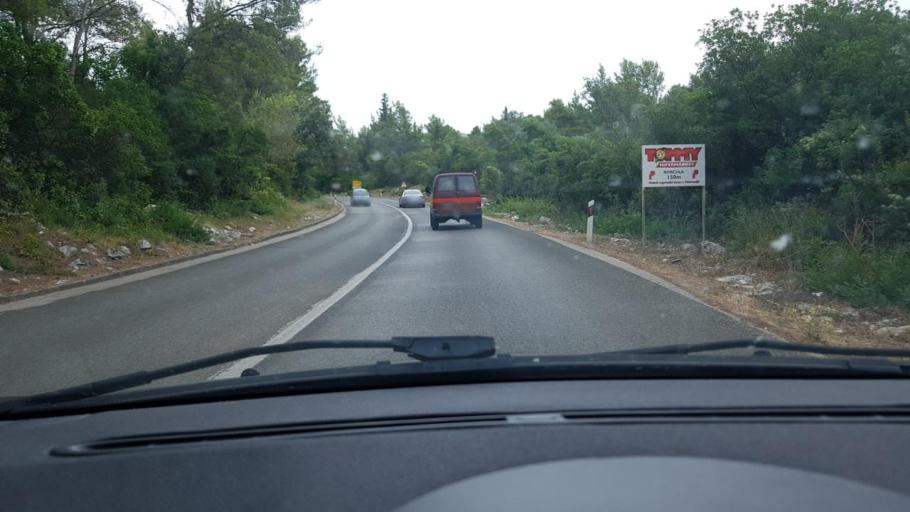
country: HR
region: Dubrovacko-Neretvanska
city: Korcula
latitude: 42.9516
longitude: 17.1316
